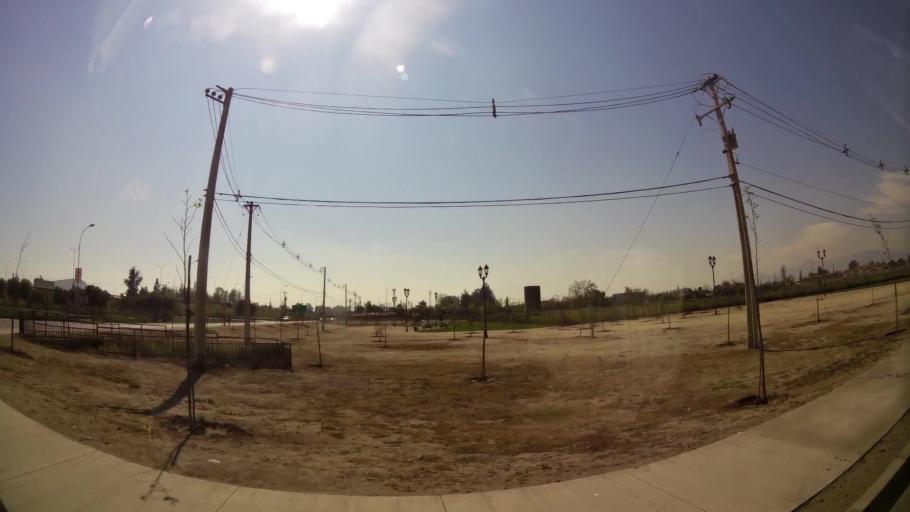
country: CL
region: Santiago Metropolitan
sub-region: Provincia de Talagante
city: Penaflor
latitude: -33.5598
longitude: -70.8276
